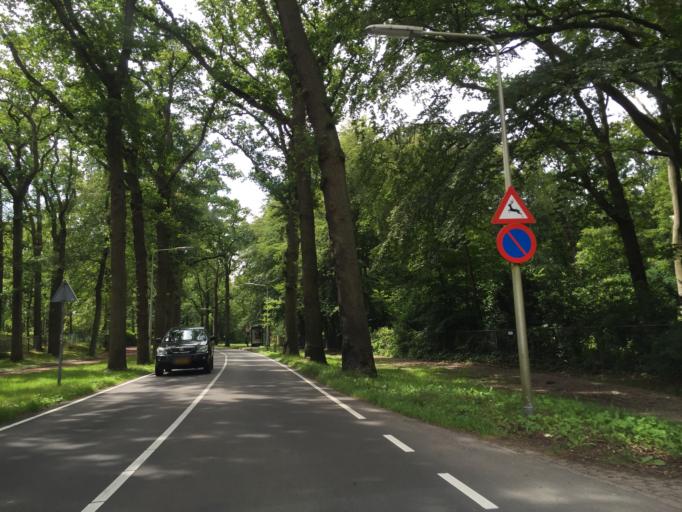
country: NL
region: South Holland
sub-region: Gemeente Wassenaar
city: Wassenaar
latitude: 52.1318
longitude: 4.3756
